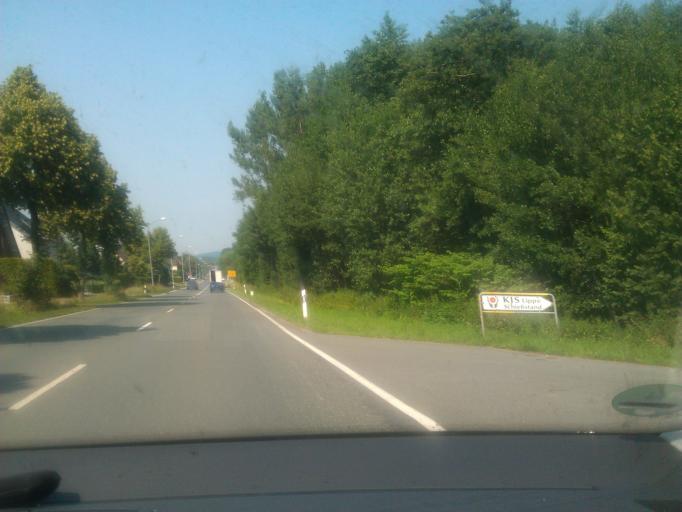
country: DE
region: North Rhine-Westphalia
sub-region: Regierungsbezirk Detmold
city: Leopoldshohe
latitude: 52.0237
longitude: 8.7141
